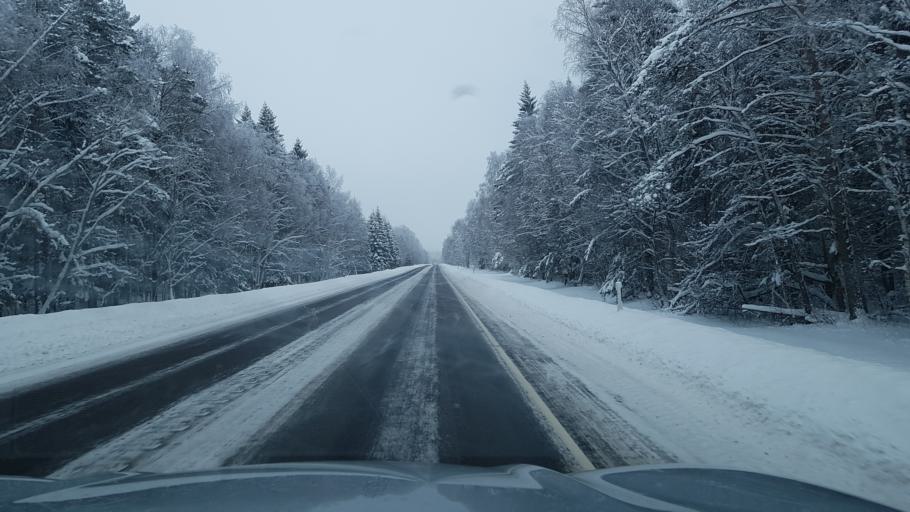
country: EE
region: Ida-Virumaa
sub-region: Johvi vald
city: Johvi
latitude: 59.3037
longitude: 27.3944
